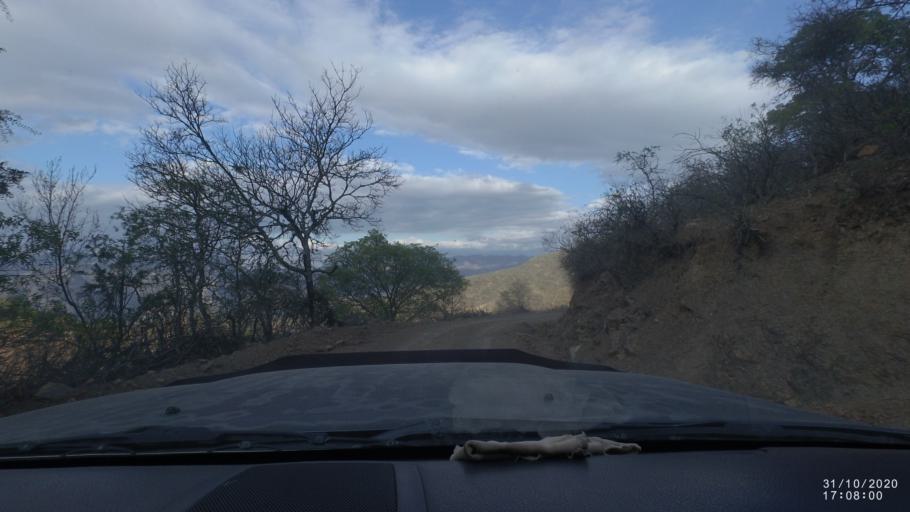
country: BO
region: Chuquisaca
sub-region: Provincia Zudanez
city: Mojocoya
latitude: -18.5457
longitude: -64.5414
